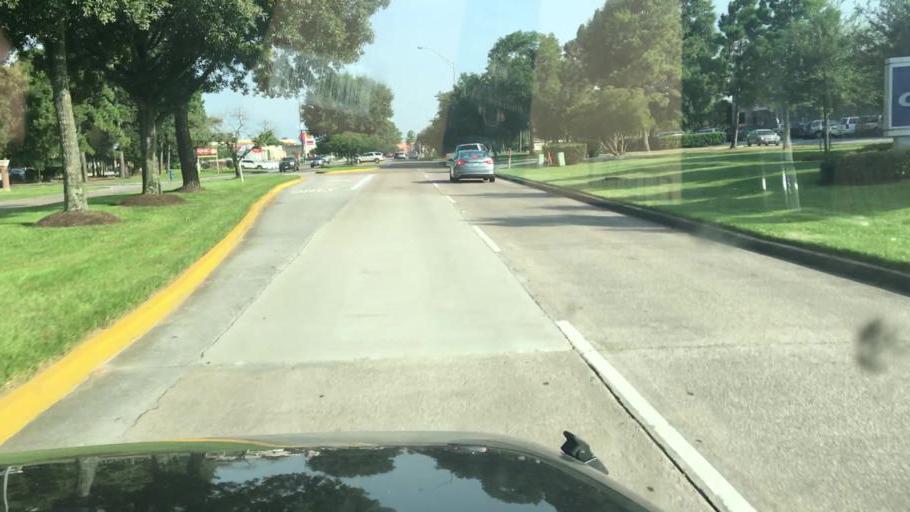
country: US
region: Texas
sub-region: Harris County
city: Atascocita
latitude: 30.0014
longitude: -95.1634
